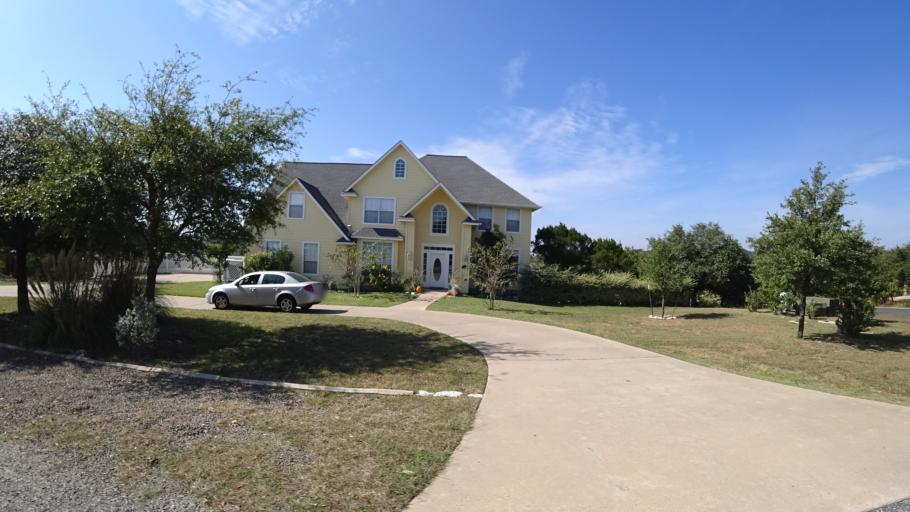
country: US
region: Texas
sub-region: Travis County
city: Bee Cave
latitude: 30.2230
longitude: -97.9360
